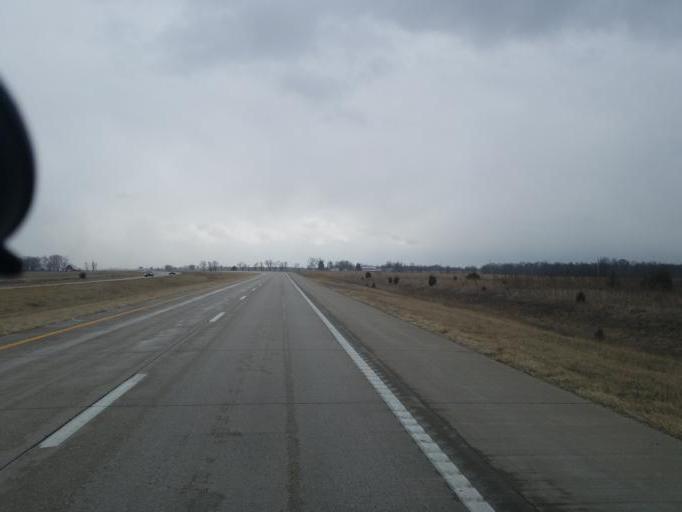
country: US
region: Missouri
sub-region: Randolph County
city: Huntsville
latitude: 39.5759
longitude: -92.4658
